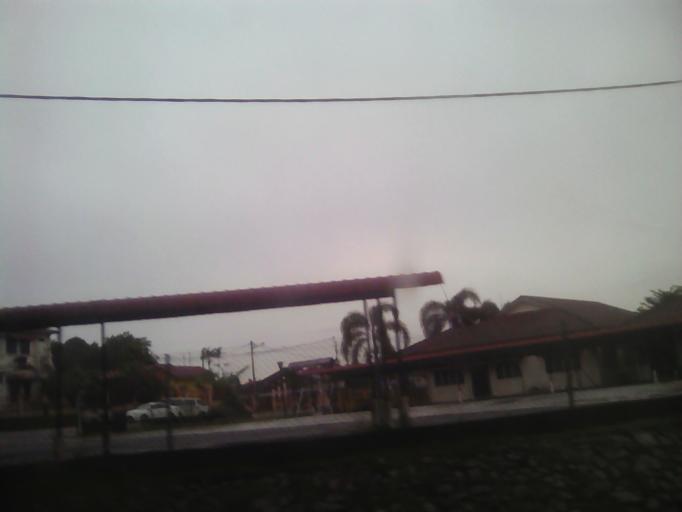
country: MY
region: Kedah
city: Kulim
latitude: 5.3686
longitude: 100.5594
